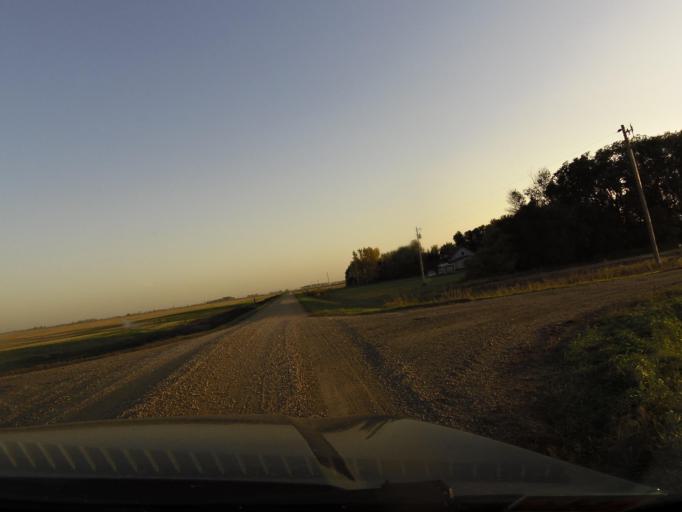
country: US
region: North Dakota
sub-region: Walsh County
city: Grafton
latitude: 48.3832
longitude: -97.2554
